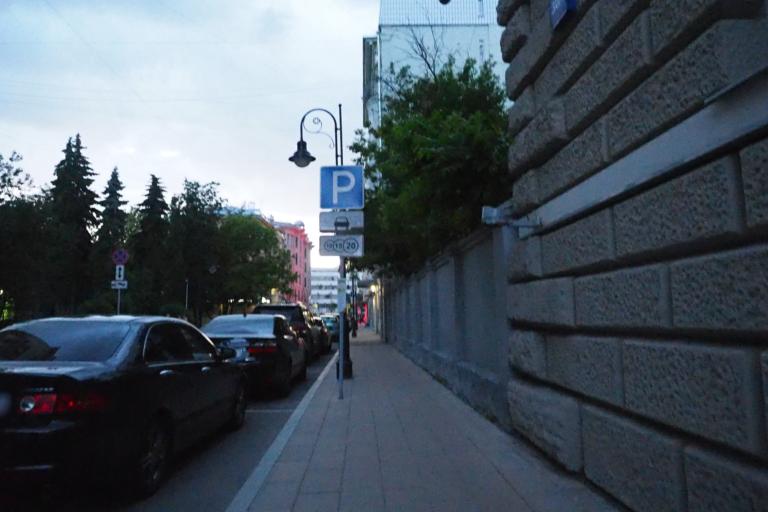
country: RU
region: Moskovskaya
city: Dorogomilovo
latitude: 55.7623
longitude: 37.5905
